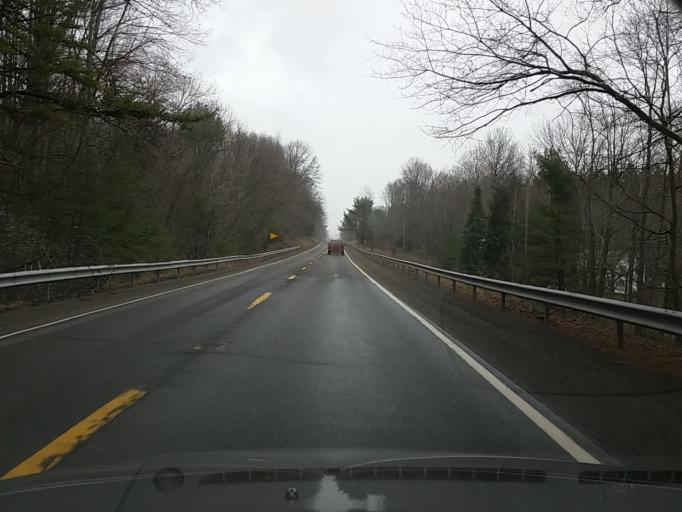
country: US
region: Pennsylvania
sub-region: Sullivan County
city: Laporte
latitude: 41.2824
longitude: -76.3453
